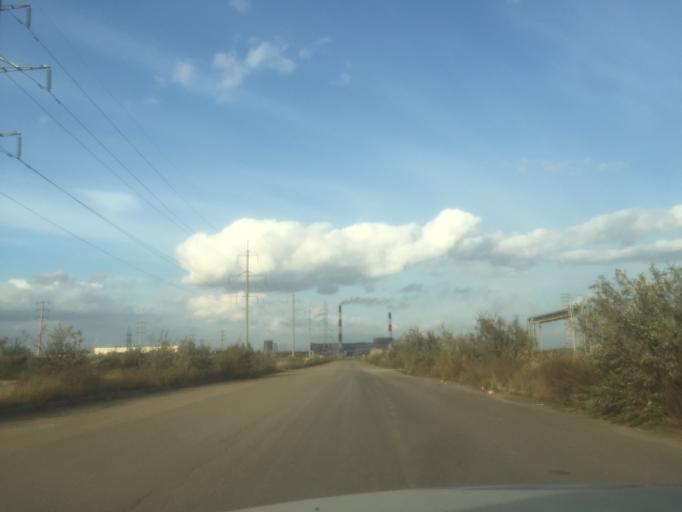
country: KZ
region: Astana Qalasy
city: Astana
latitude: 51.1729
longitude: 71.4947
